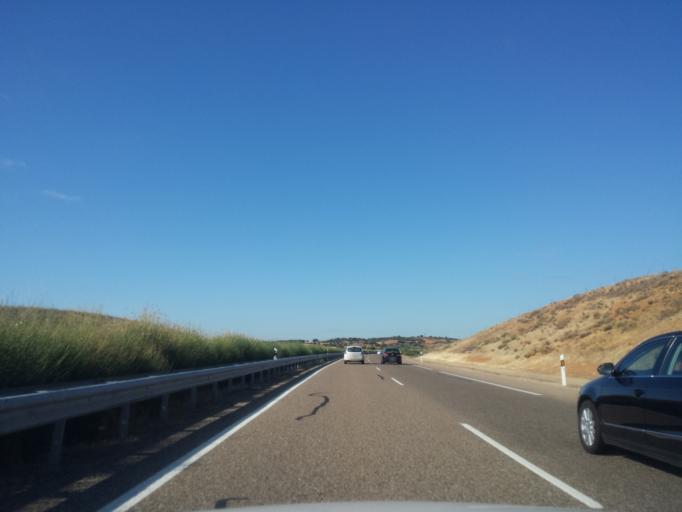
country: ES
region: Castille and Leon
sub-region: Provincia de Leon
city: Villamandos
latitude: 42.1953
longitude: -5.6065
